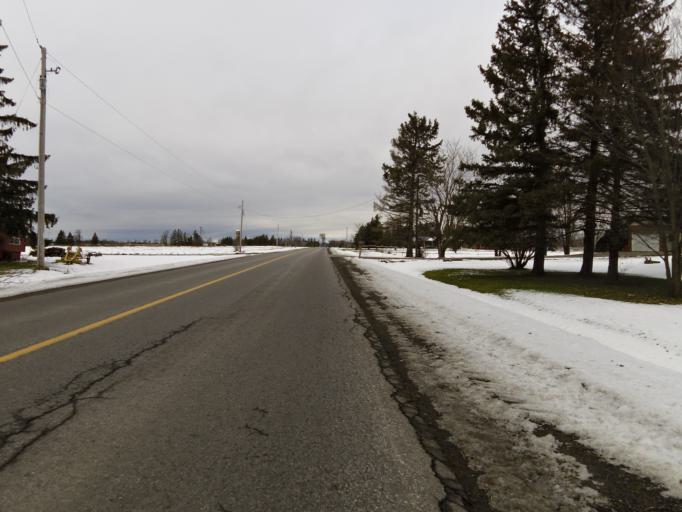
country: CA
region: Ontario
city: Carleton Place
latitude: 45.3478
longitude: -76.0855
